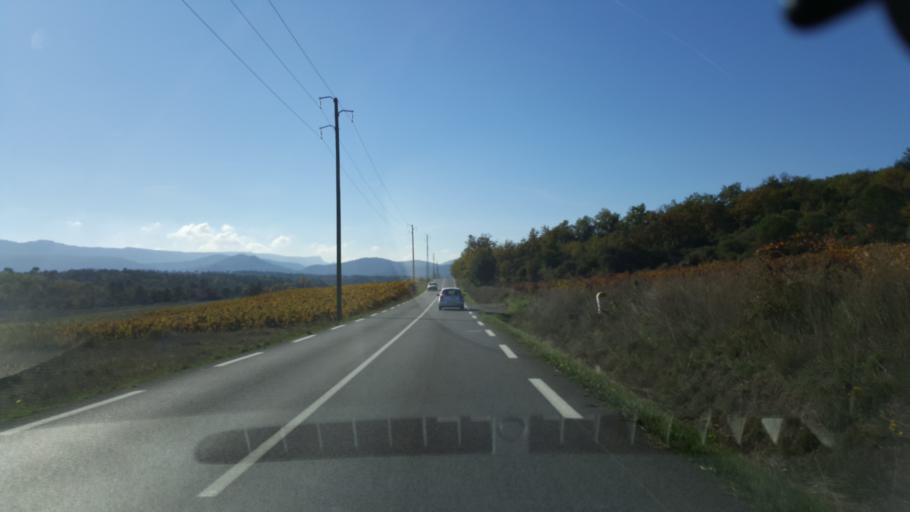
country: FR
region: Provence-Alpes-Cote d'Azur
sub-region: Departement du Var
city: Rougiers
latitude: 43.4044
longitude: 5.8161
